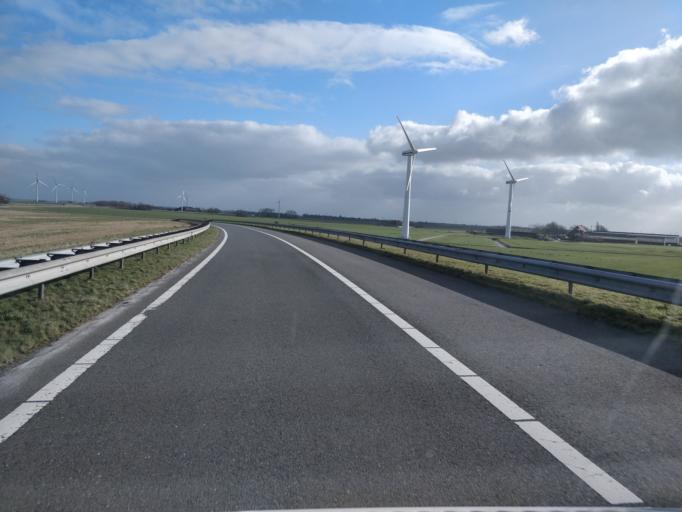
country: NL
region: Friesland
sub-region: Sudwest Fryslan
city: Makkum
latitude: 53.0967
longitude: 5.3937
